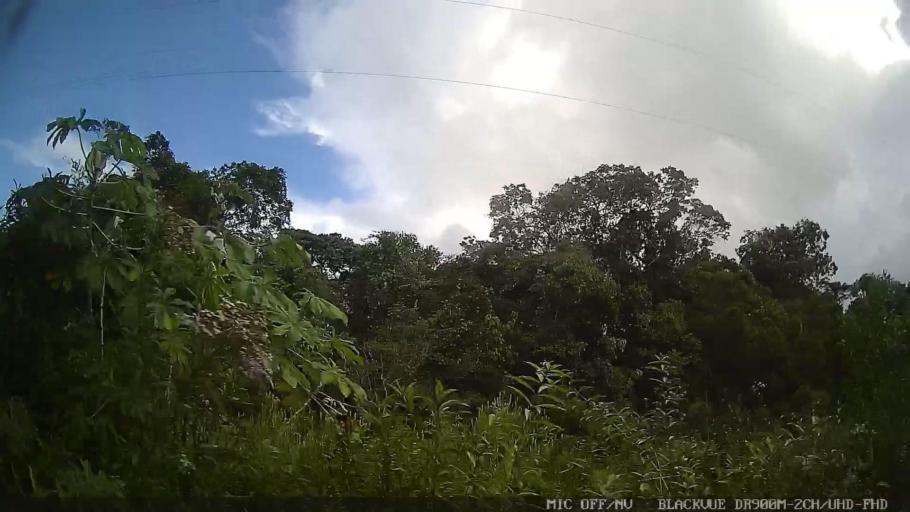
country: BR
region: Sao Paulo
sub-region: Itanhaem
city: Itanhaem
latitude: -24.1761
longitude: -46.9255
